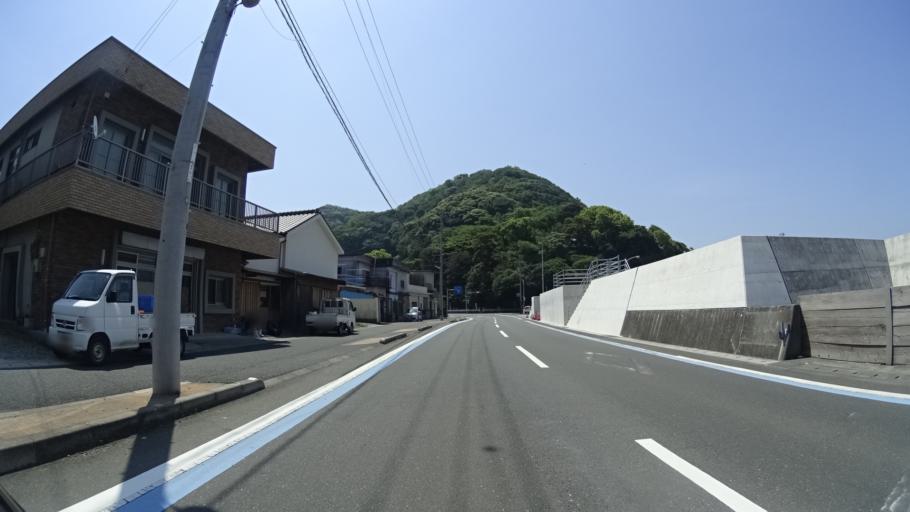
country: JP
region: Ehime
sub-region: Nishiuwa-gun
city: Ikata-cho
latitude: 33.3889
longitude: 132.1208
